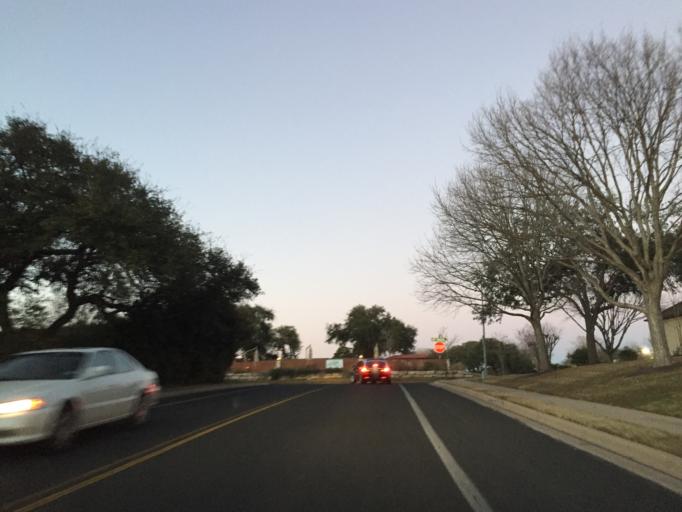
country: US
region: Texas
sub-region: Williamson County
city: Jollyville
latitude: 30.4016
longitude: -97.7677
